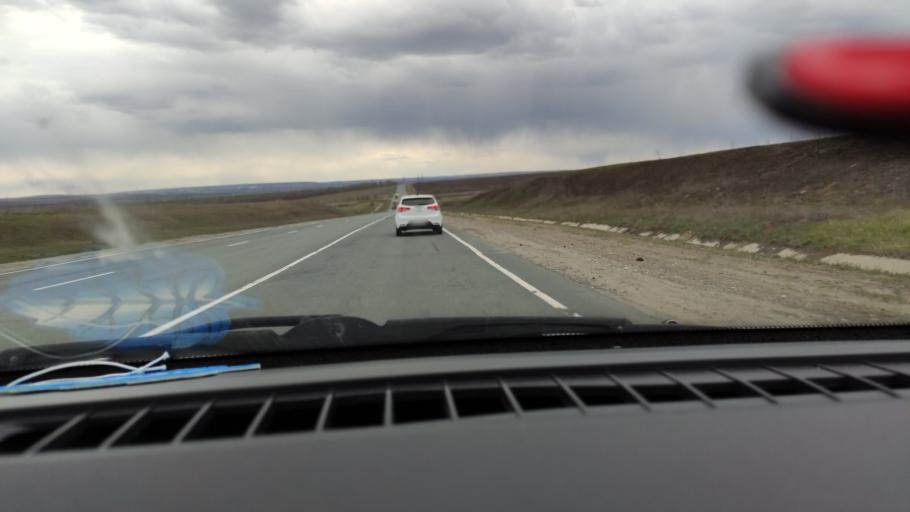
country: RU
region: Saratov
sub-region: Saratovskiy Rayon
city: Saratov
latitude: 51.7561
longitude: 46.0658
